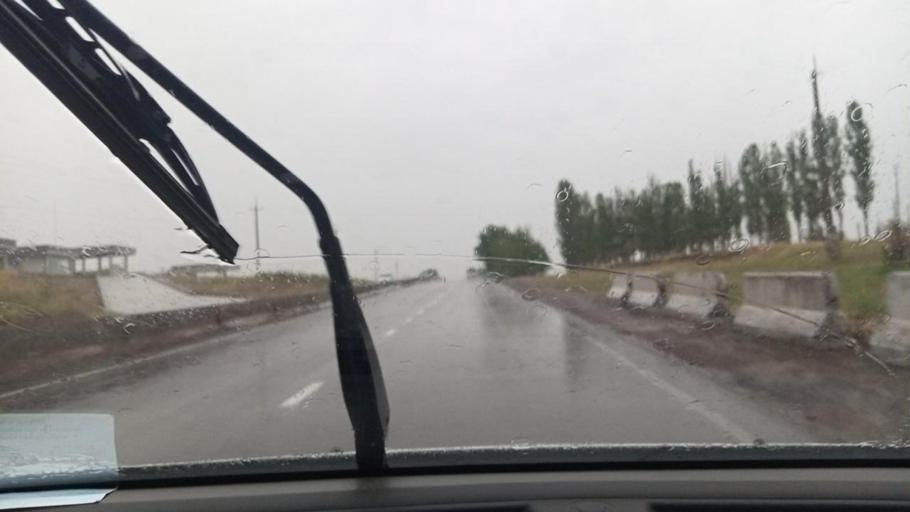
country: UZ
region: Toshkent
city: Ohangaron
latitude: 40.9353
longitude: 69.8901
